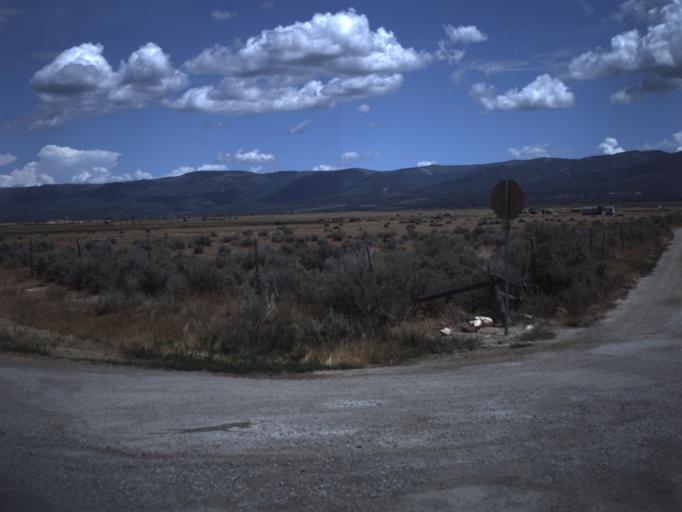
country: US
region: Utah
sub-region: Sanpete County
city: Mount Pleasant
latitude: 39.4991
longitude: -111.4899
